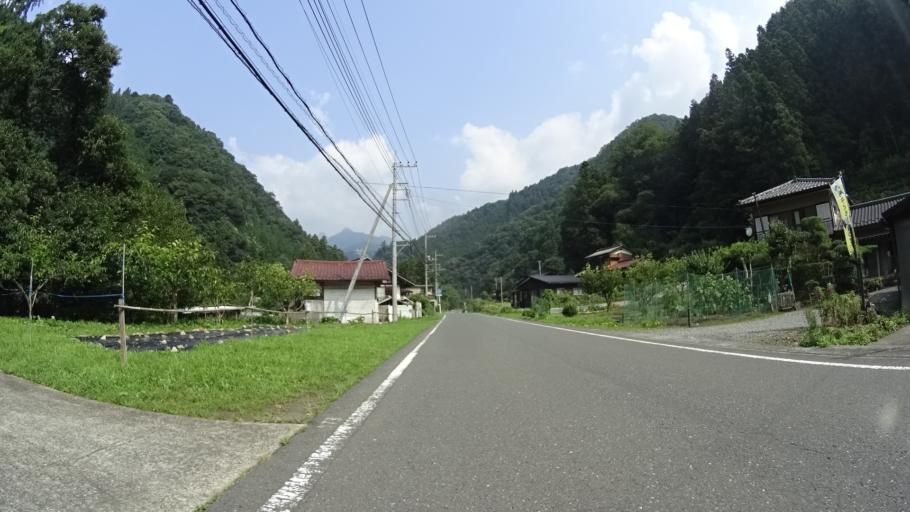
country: JP
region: Saitama
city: Chichibu
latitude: 36.0417
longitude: 138.8942
